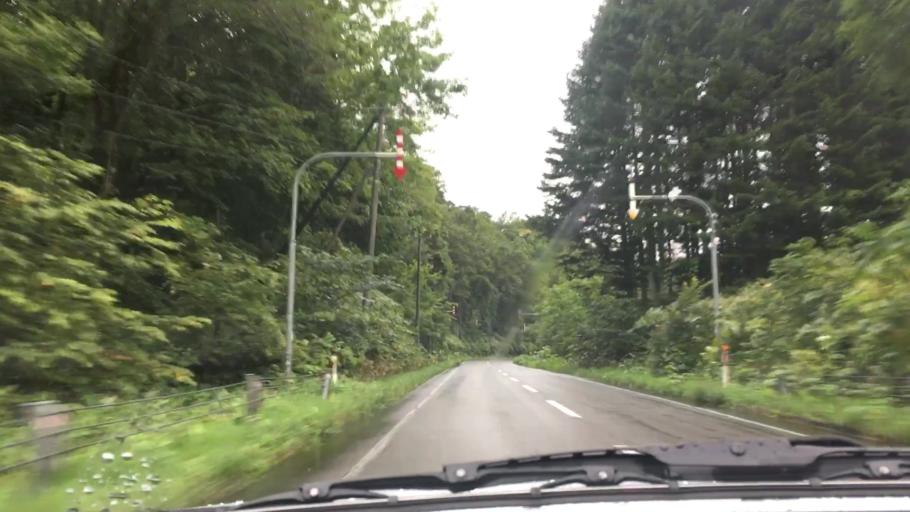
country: JP
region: Hokkaido
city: Niseko Town
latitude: 42.6310
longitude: 140.7243
